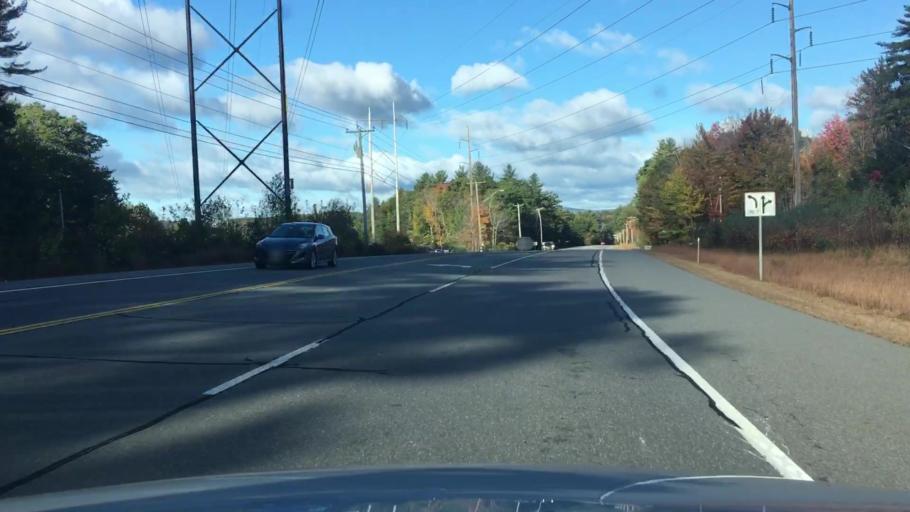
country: US
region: New Hampshire
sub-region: Strafford County
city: Lee
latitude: 43.1542
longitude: -71.0564
